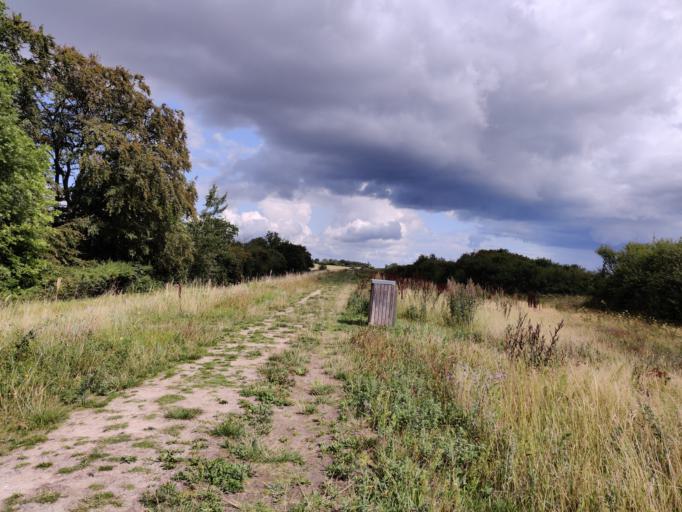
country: DK
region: Zealand
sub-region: Guldborgsund Kommune
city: Nykobing Falster
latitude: 54.7182
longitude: 12.0046
